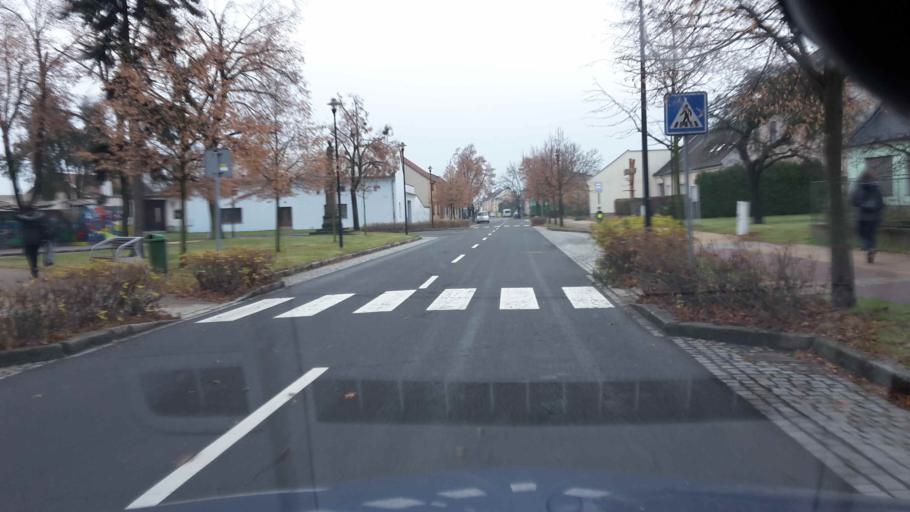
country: CZ
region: Olomoucky
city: Grygov
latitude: 49.5711
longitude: 17.2960
